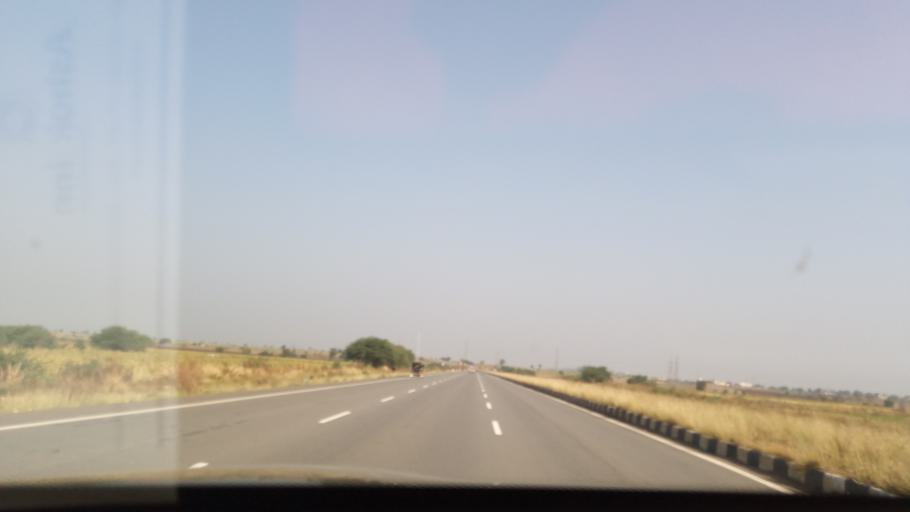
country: IN
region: Karnataka
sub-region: Haveri
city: Haveri
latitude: 14.7994
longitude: 75.3781
